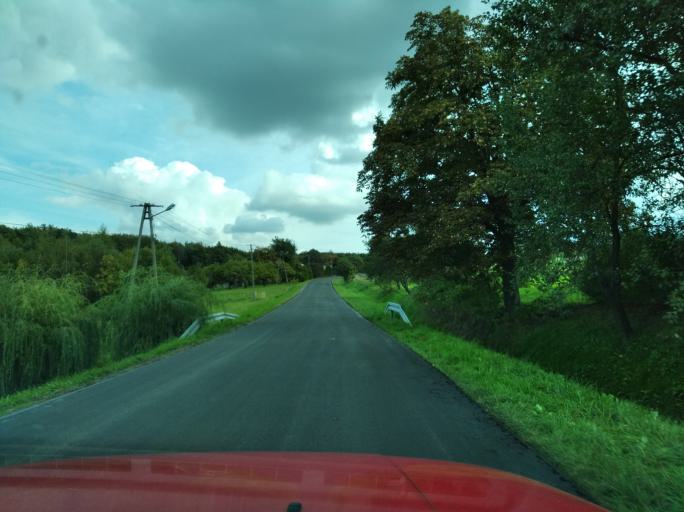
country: PL
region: Subcarpathian Voivodeship
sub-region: Powiat rzeszowski
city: Straszydle
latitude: 49.9343
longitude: 21.9831
